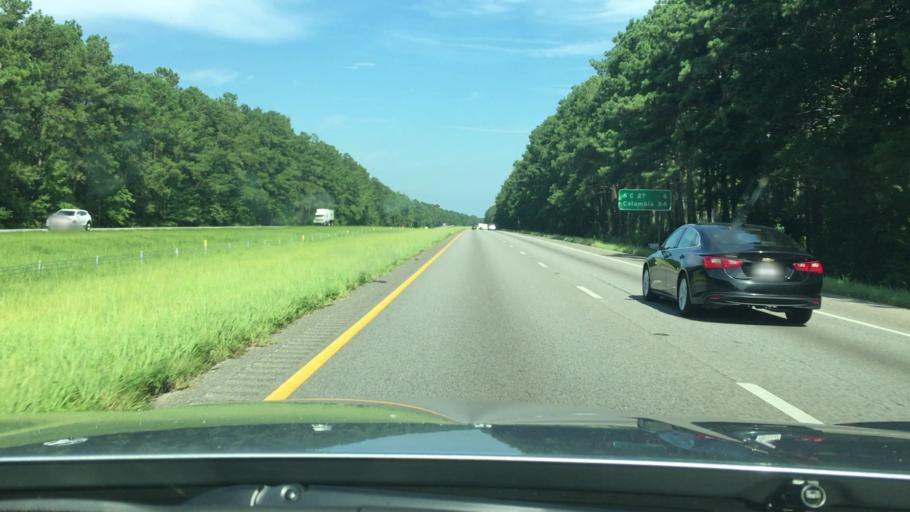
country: US
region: South Carolina
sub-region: Dorchester County
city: Summerville
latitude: 33.0876
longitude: -80.2180
